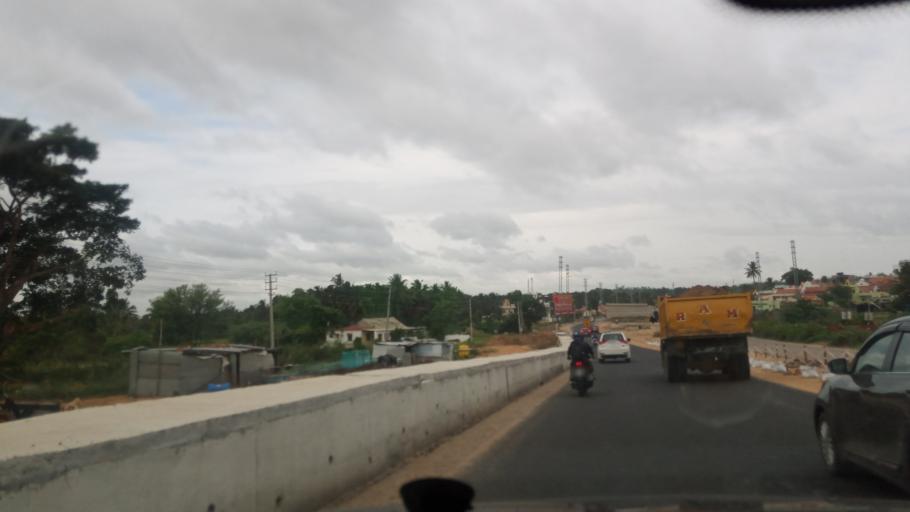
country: IN
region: Karnataka
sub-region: Mandya
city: Shrirangapattana
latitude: 12.4702
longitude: 76.7578
